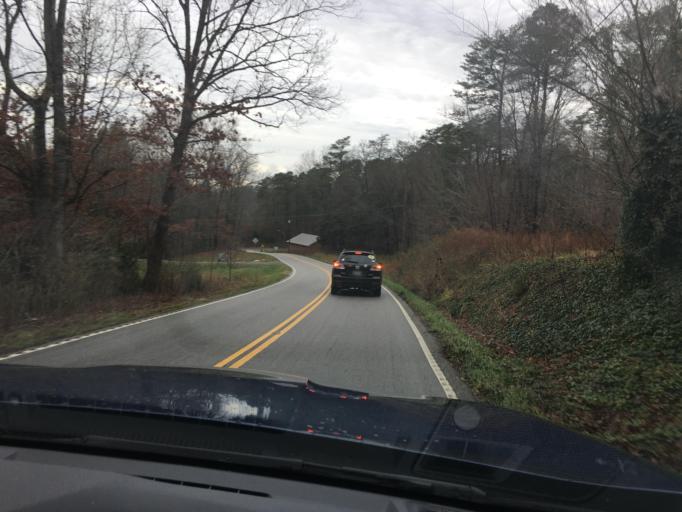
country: US
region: Tennessee
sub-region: McMinn County
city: Englewood
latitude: 35.3484
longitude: -84.4005
